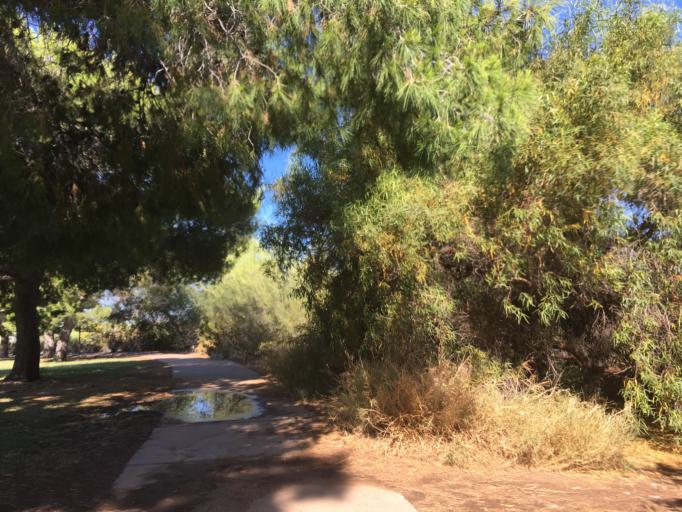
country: US
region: Arizona
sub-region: Maricopa County
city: Phoenix
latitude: 33.5341
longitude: -112.0376
